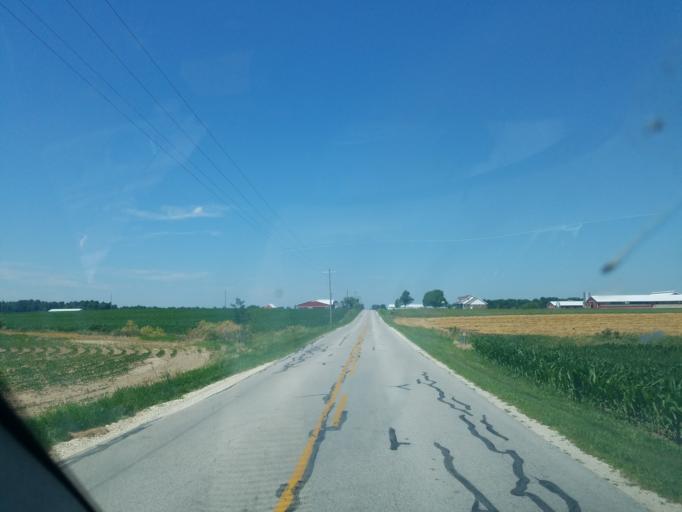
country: US
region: Ohio
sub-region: Mercer County
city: Saint Henry
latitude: 40.4506
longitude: -84.6855
